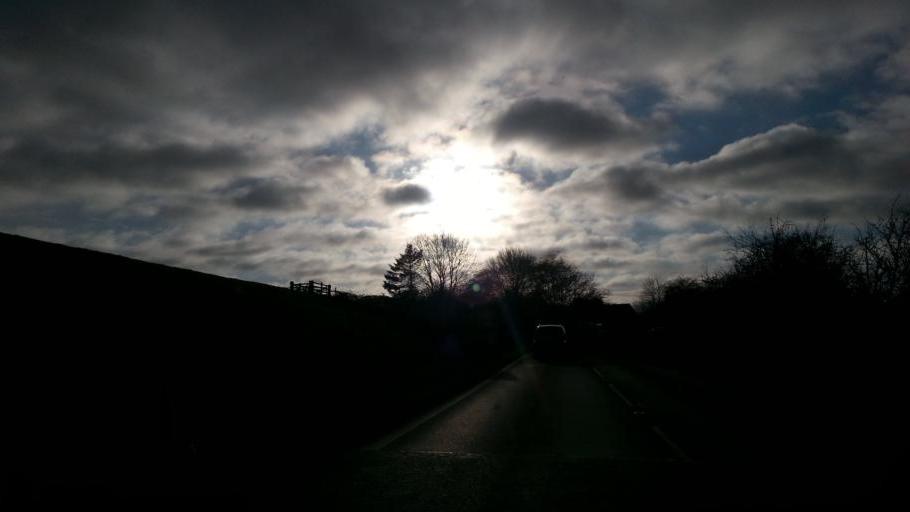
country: GB
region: England
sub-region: Norfolk
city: Downham Market
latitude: 52.5925
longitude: 0.3425
